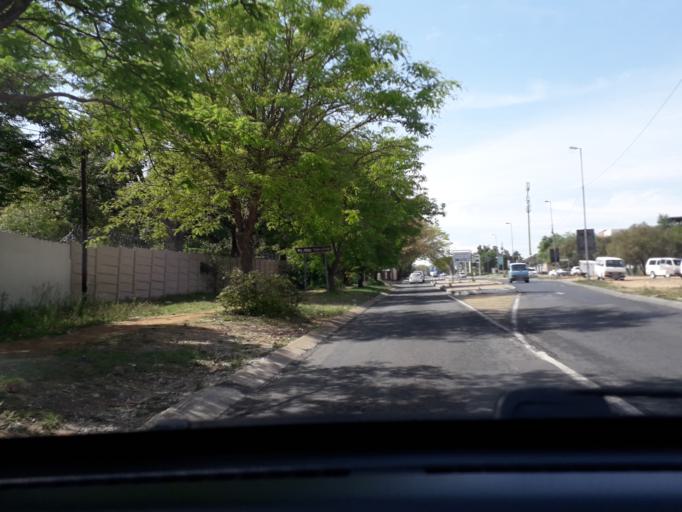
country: ZA
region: Gauteng
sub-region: City of Johannesburg Metropolitan Municipality
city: Midrand
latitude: -26.0636
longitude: 28.0737
